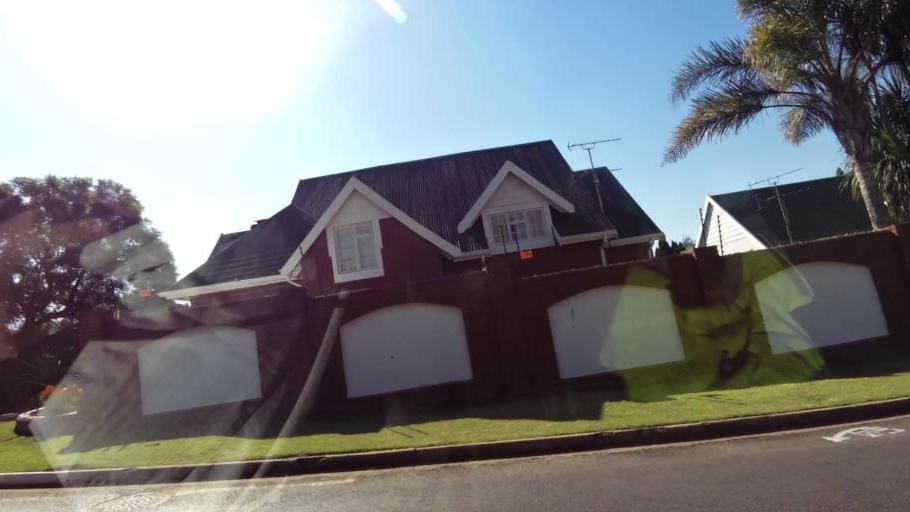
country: ZA
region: Gauteng
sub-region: City of Johannesburg Metropolitan Municipality
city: Roodepoort
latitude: -26.1348
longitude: 27.9483
